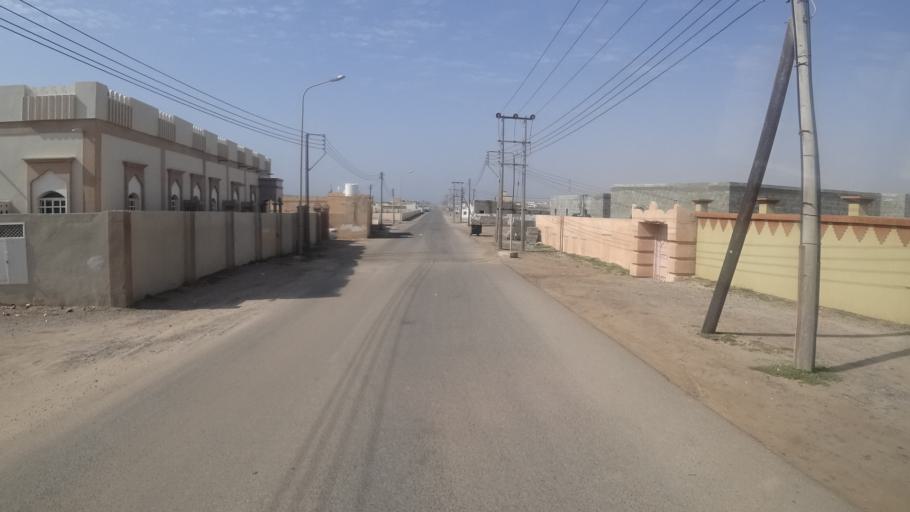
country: OM
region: Ash Sharqiyah
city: Sur
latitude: 22.1828
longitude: 59.7635
